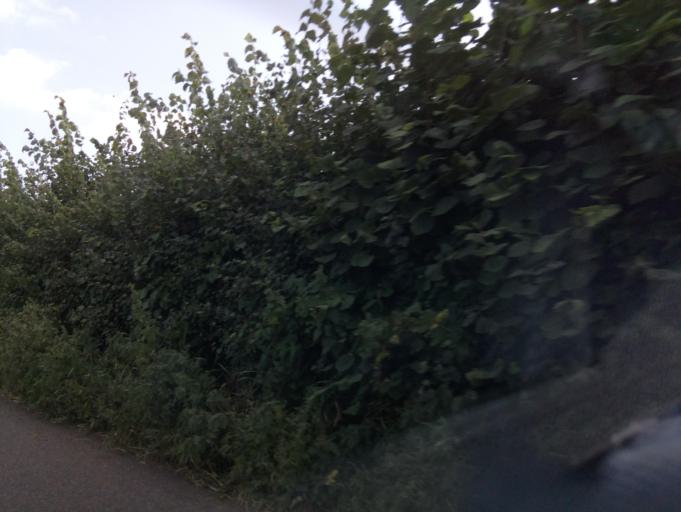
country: GB
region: England
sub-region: Devon
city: Tiverton
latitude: 50.8321
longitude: -3.4989
